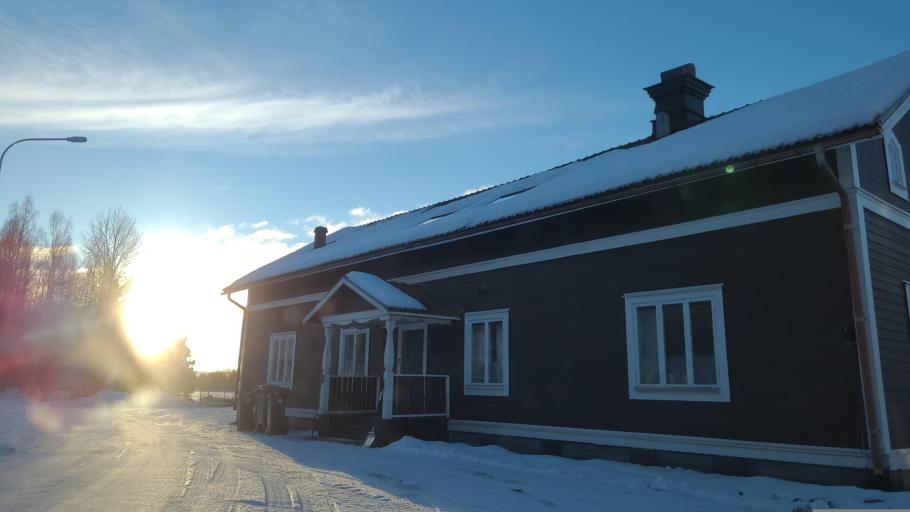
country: SE
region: Gaevleborg
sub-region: Bollnas Kommun
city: Bollnas
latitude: 61.3522
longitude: 16.4082
